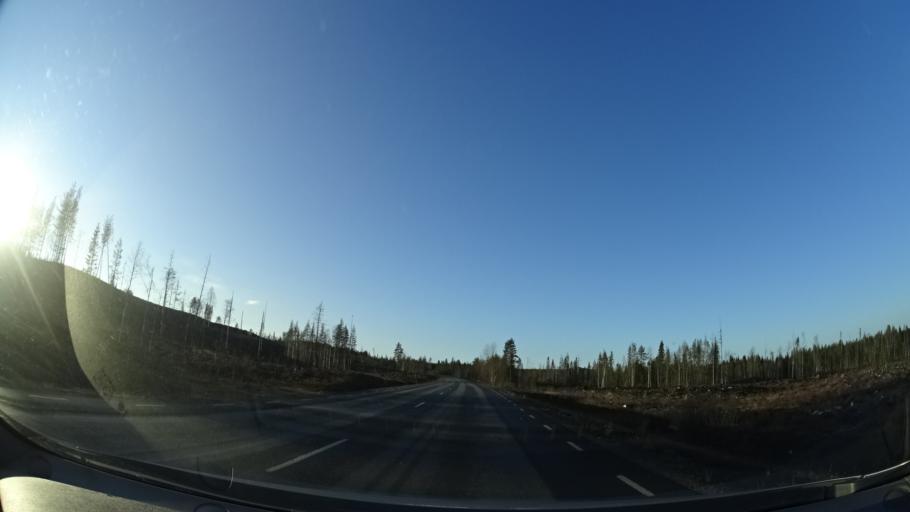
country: SE
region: Vaesterbotten
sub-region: Norsjo Kommun
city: Norsjoe
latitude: 64.9865
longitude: 19.4689
